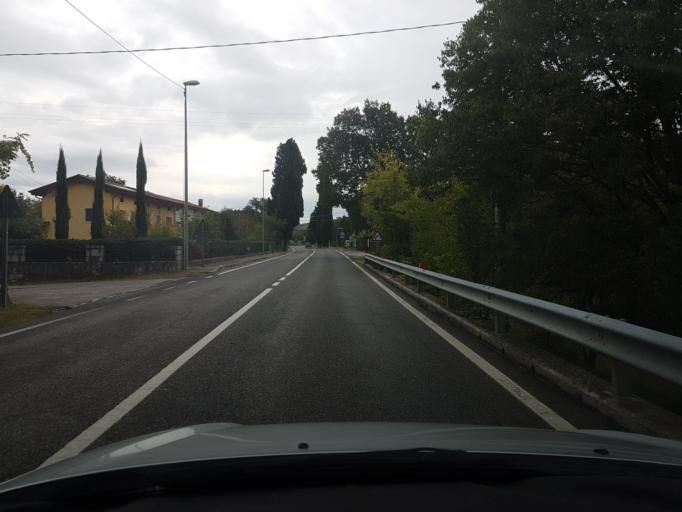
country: IT
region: Friuli Venezia Giulia
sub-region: Provincia di Gorizia
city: Doberdo del Lago
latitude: 45.8218
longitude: 13.5790
